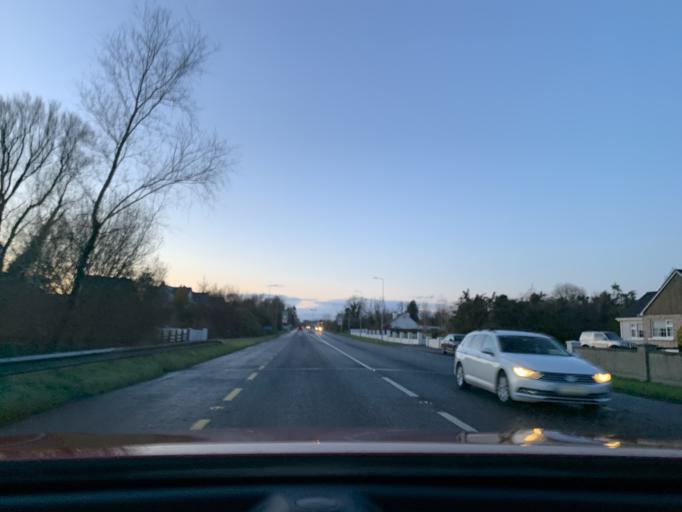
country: IE
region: Connaught
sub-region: County Leitrim
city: Carrick-on-Shannon
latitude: 53.9415
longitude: -8.0663
